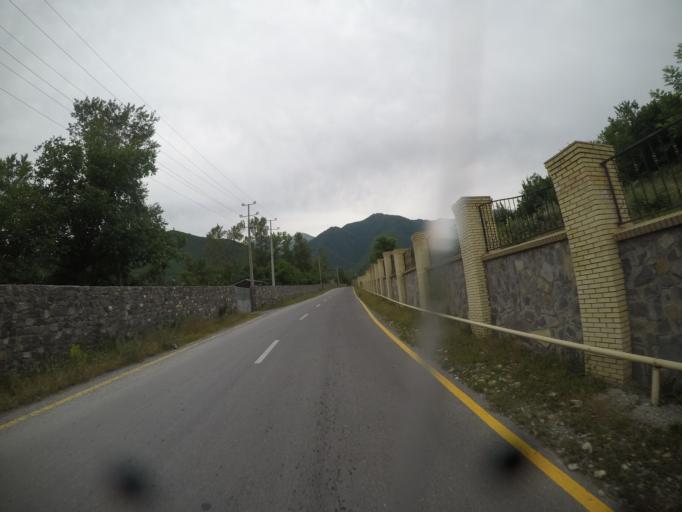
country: AZ
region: Shaki City
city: Sheki
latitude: 41.2469
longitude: 47.2012
